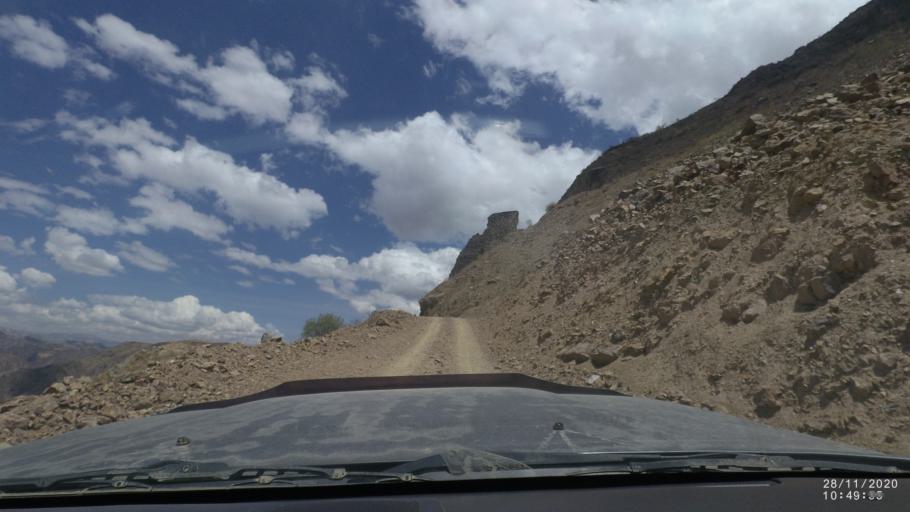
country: BO
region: Cochabamba
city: Capinota
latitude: -17.7854
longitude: -66.1228
